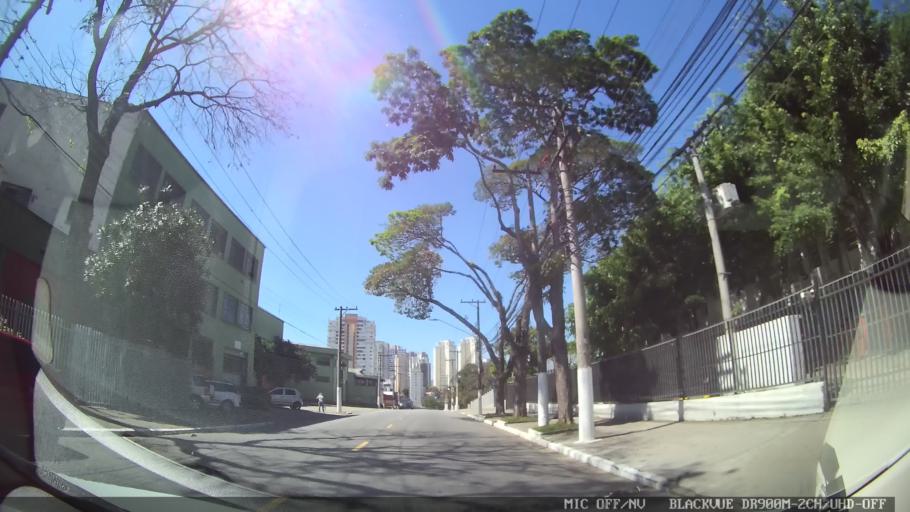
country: BR
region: Sao Paulo
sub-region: Sao Paulo
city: Sao Paulo
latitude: -23.5000
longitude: -46.6473
